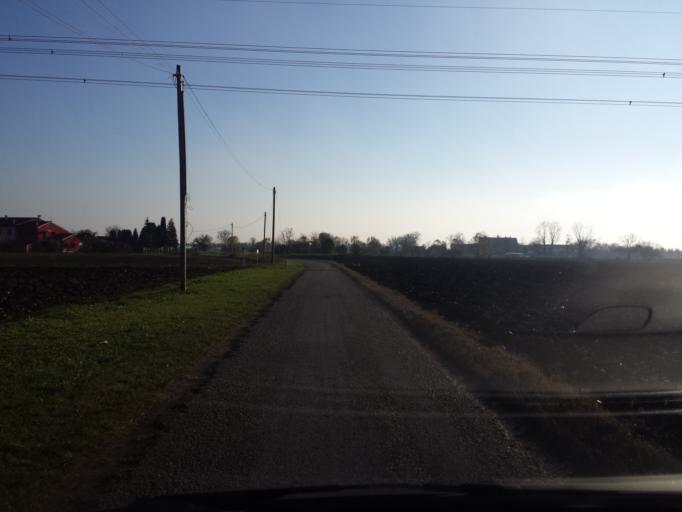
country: IT
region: Veneto
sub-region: Provincia di Vicenza
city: Sandrigo
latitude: 45.6785
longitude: 11.5846
